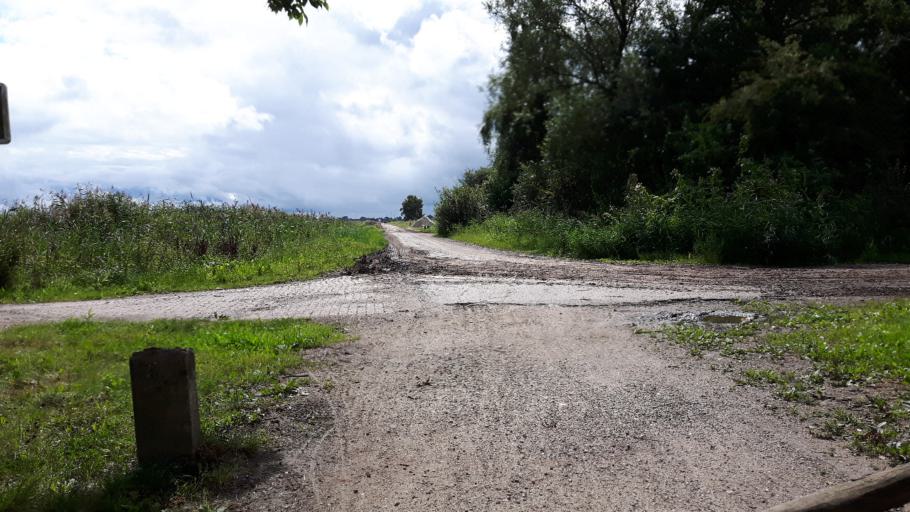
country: NL
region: Groningen
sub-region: Gemeente Slochteren
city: Slochteren
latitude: 53.2640
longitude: 6.8053
